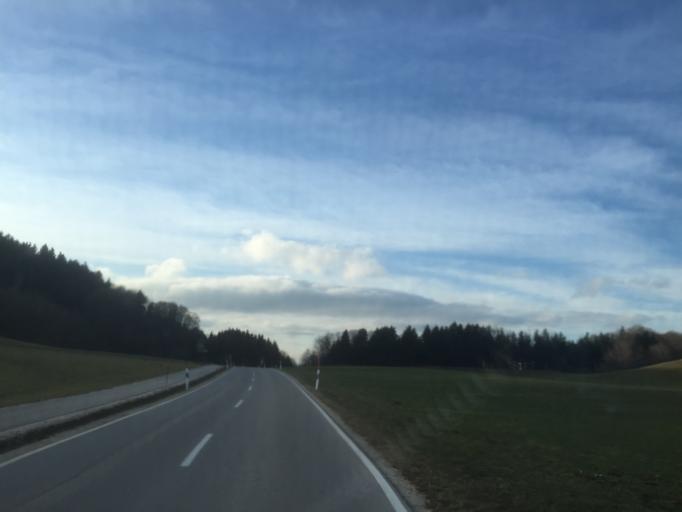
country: DE
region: Bavaria
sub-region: Upper Bavaria
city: Vachendorf
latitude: 47.8366
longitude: 12.6214
